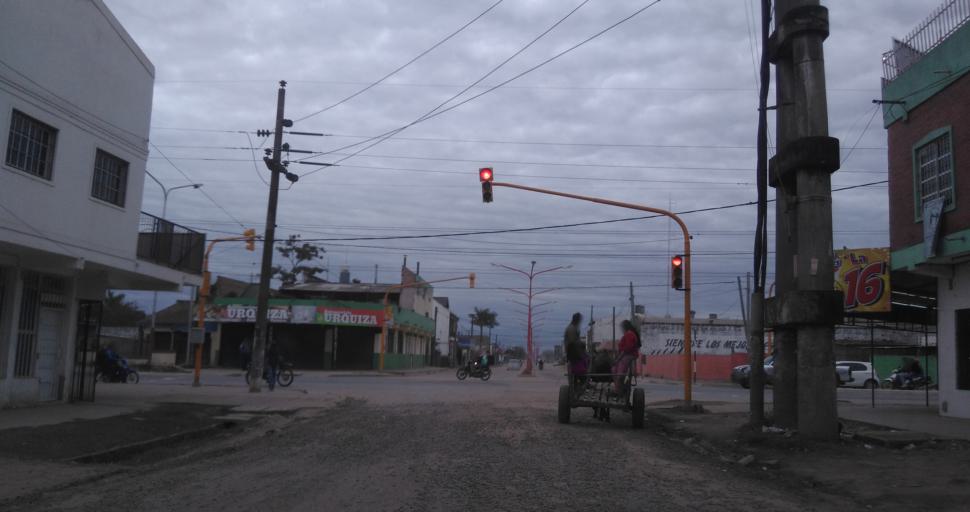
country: AR
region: Chaco
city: Resistencia
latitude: -27.4763
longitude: -58.9718
